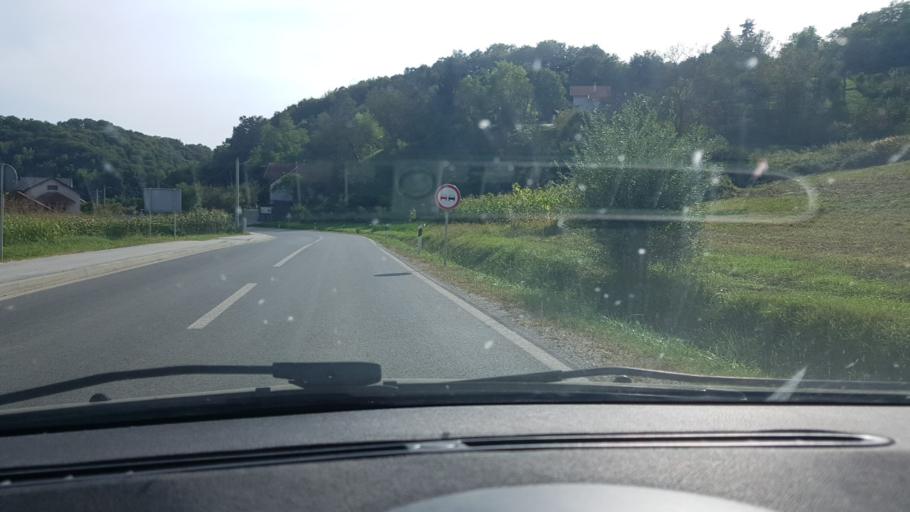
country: HR
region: Krapinsko-Zagorska
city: Zlatar
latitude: 46.0989
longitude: 16.0552
